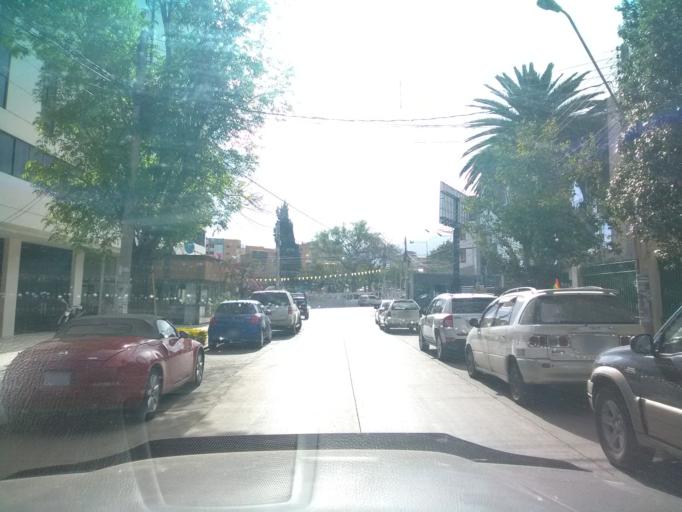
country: BO
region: Cochabamba
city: Cochabamba
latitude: -17.3690
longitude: -66.1630
